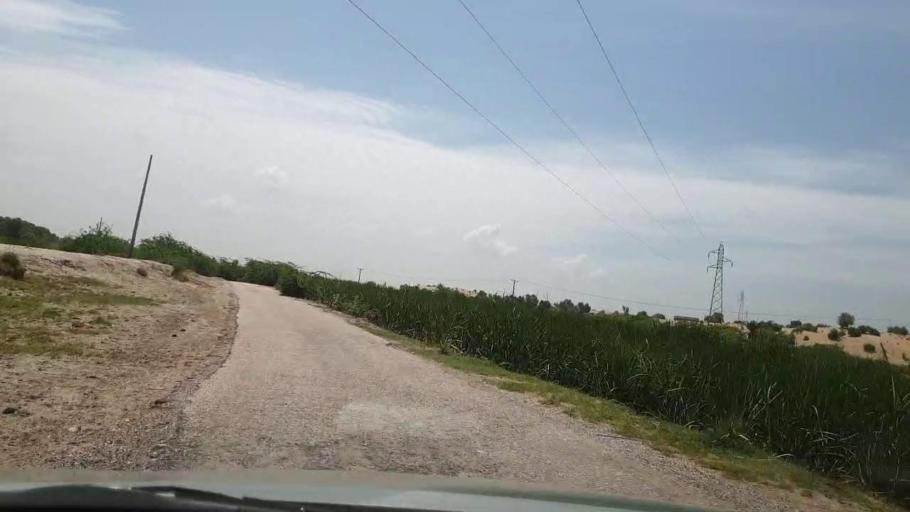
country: PK
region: Sindh
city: Bozdar
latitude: 27.0788
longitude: 68.9661
